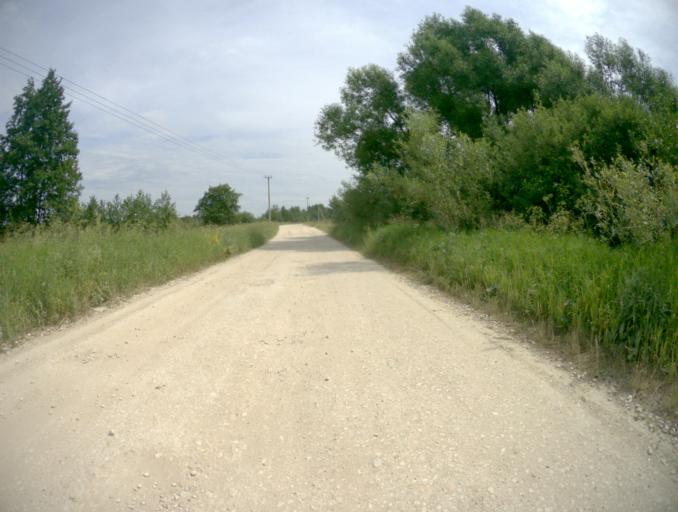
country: RU
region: Vladimir
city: Raduzhnyy
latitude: 56.0281
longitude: 40.2956
